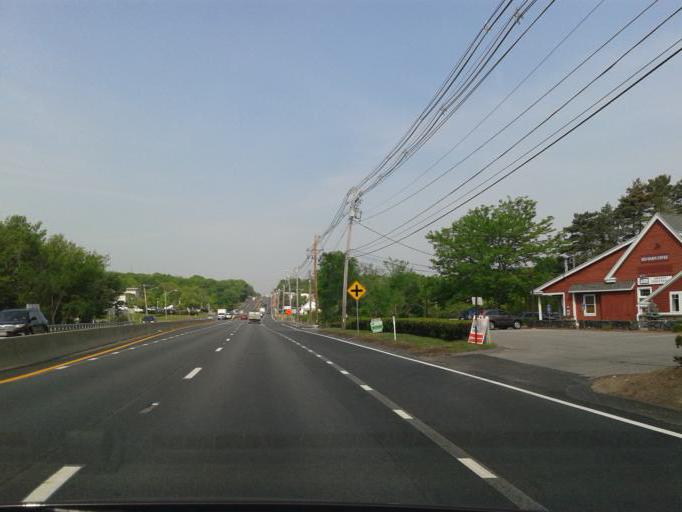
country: US
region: Massachusetts
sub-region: Worcester County
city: Southborough
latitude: 42.2915
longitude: -71.5290
